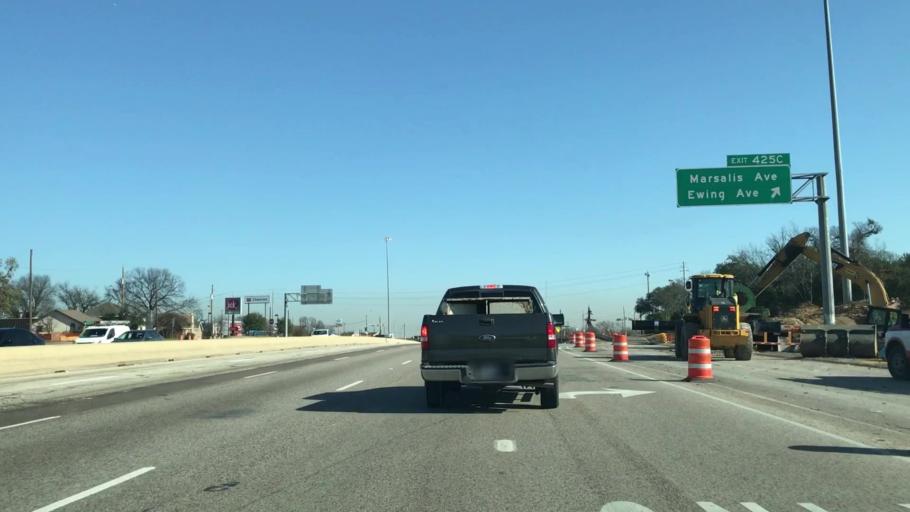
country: US
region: Texas
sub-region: Dallas County
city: Dallas
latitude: 32.7423
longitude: -96.8183
